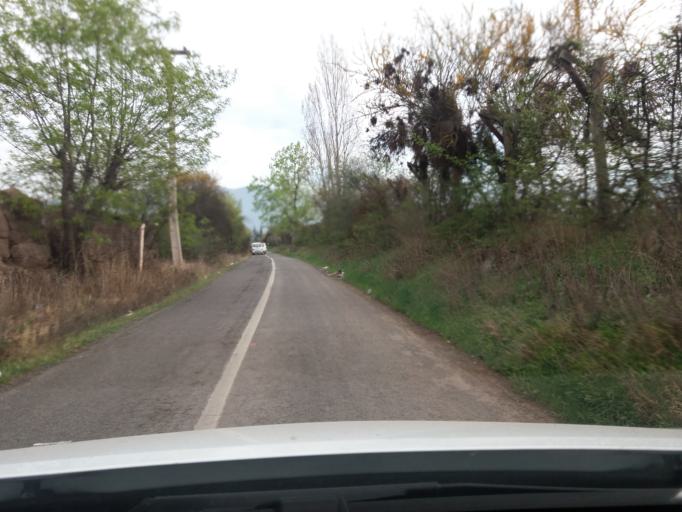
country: CL
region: Valparaiso
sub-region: Provincia de Los Andes
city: Los Andes
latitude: -32.8248
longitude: -70.6407
